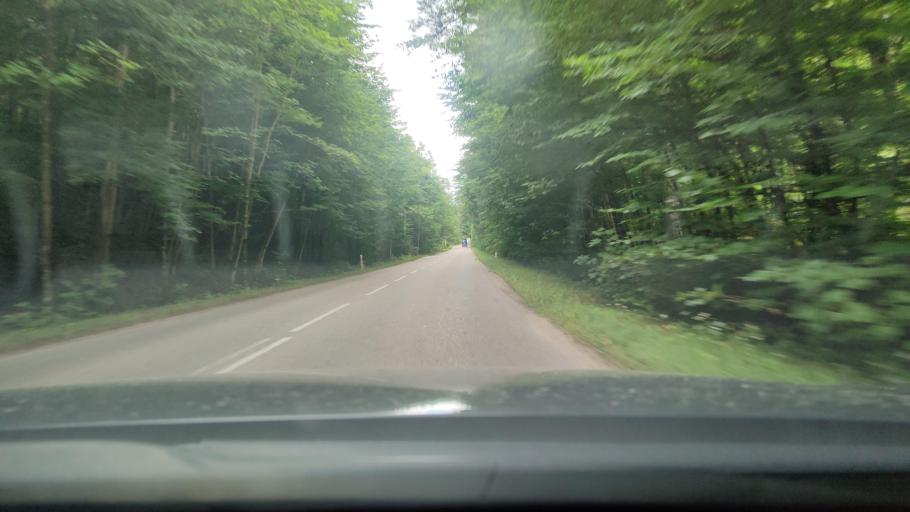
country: PL
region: Pomeranian Voivodeship
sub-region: Powiat pucki
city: Krokowa
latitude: 54.7223
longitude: 18.1718
